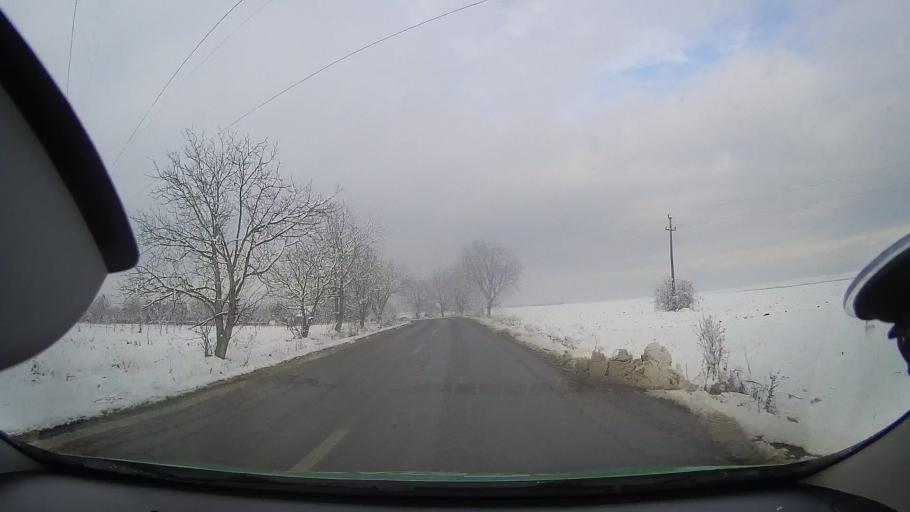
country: RO
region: Mures
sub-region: Comuna Atintis
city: Atintis
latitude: 46.4421
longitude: 24.0918
